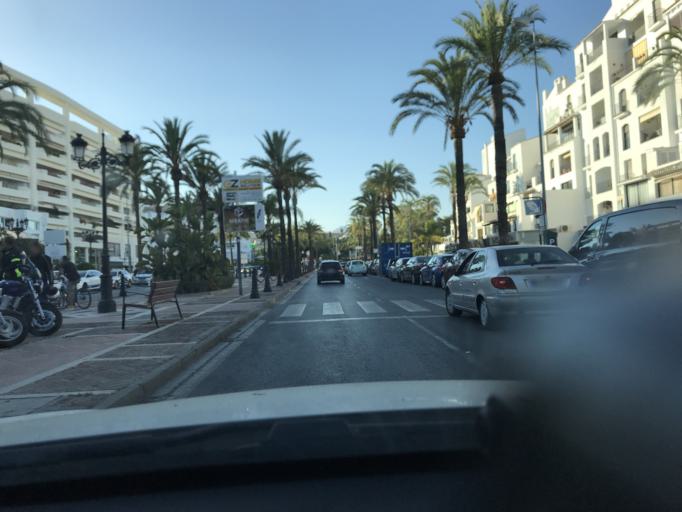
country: ES
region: Andalusia
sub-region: Provincia de Malaga
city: Marbella
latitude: 36.4870
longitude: -4.9558
